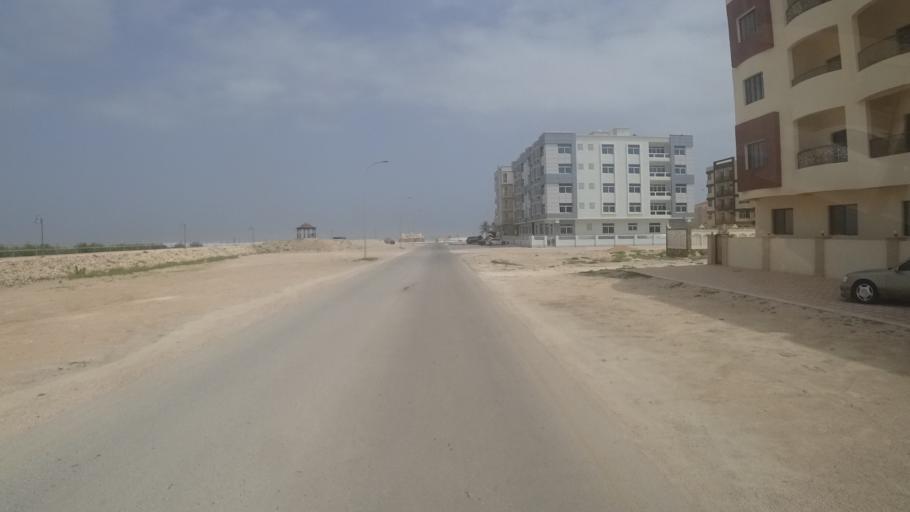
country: OM
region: Zufar
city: Salalah
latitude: 17.0136
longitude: 54.1752
